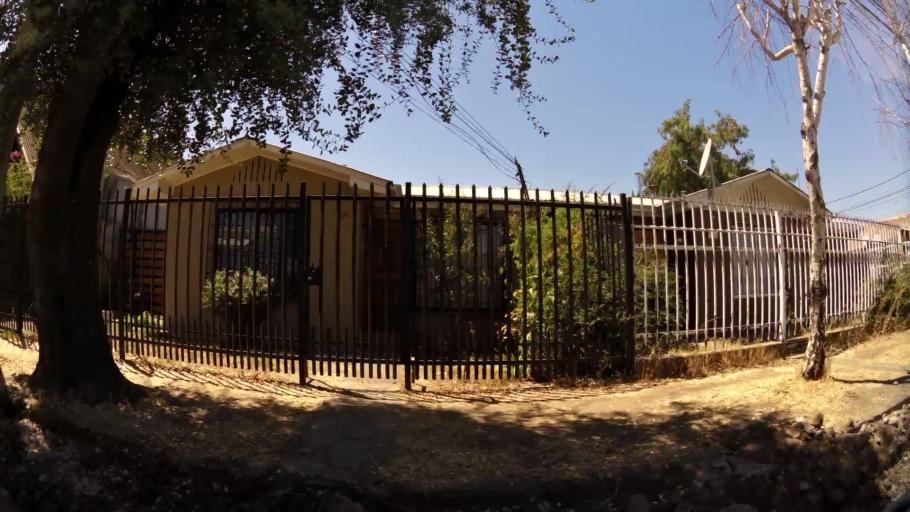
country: CL
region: Maule
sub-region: Provincia de Curico
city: Curico
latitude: -34.9775
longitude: -71.2200
